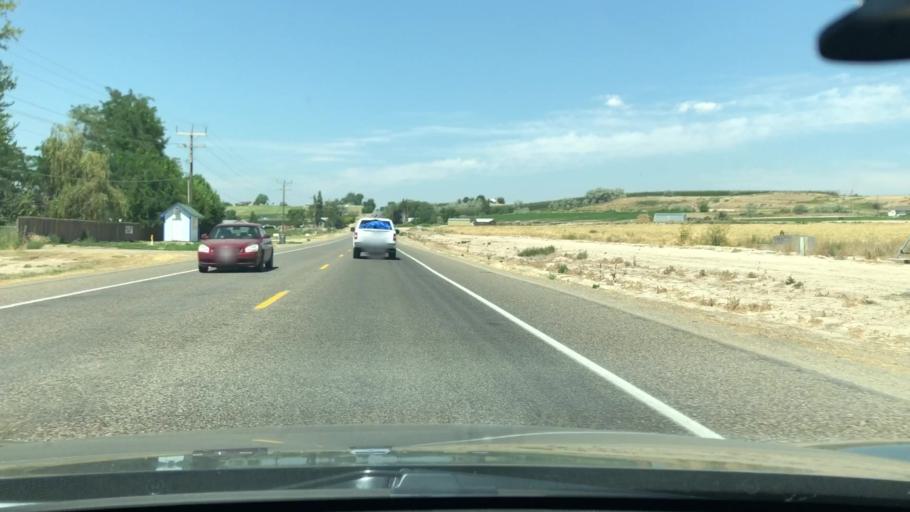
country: US
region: Idaho
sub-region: Canyon County
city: Wilder
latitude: 43.6499
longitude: -116.9116
